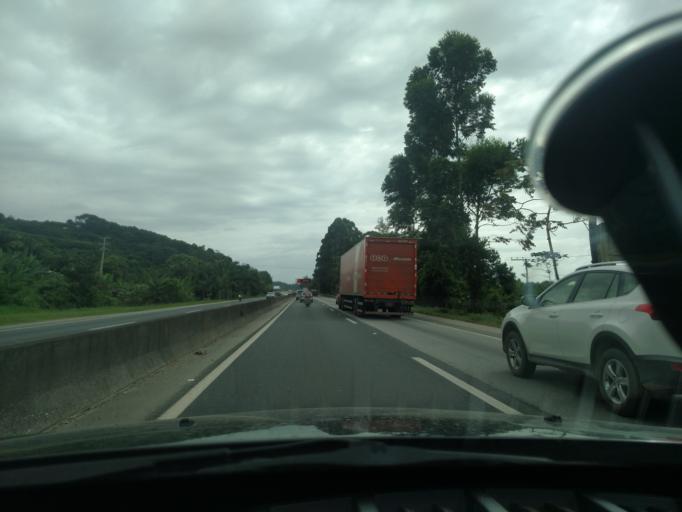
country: BR
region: Santa Catarina
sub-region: Itapema
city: Itapema
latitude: -27.0797
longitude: -48.6001
